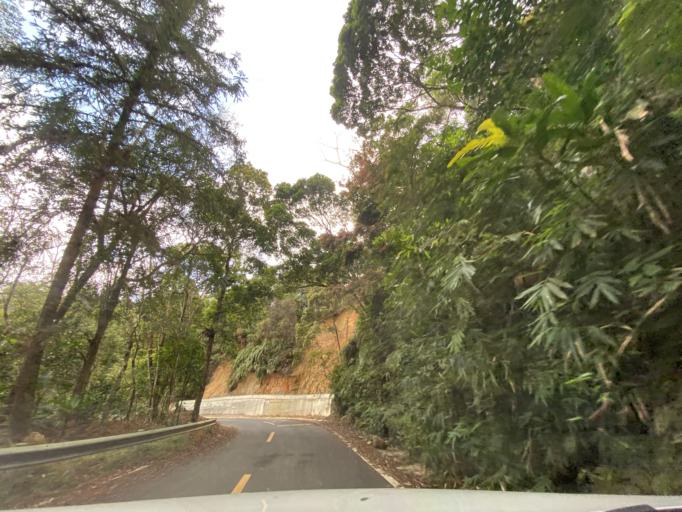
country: CN
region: Hainan
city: Diaoluoshan
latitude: 18.7020
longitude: 109.8820
